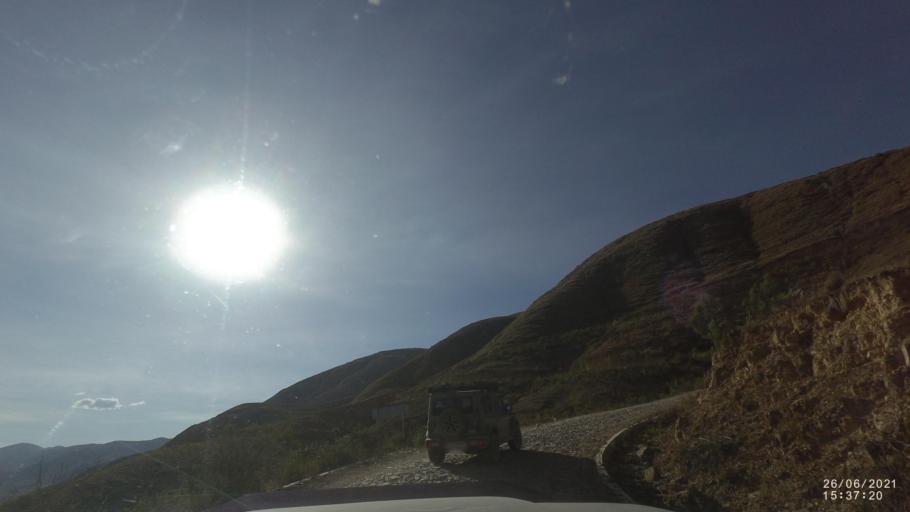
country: BO
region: Cochabamba
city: Mizque
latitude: -17.9129
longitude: -65.6880
